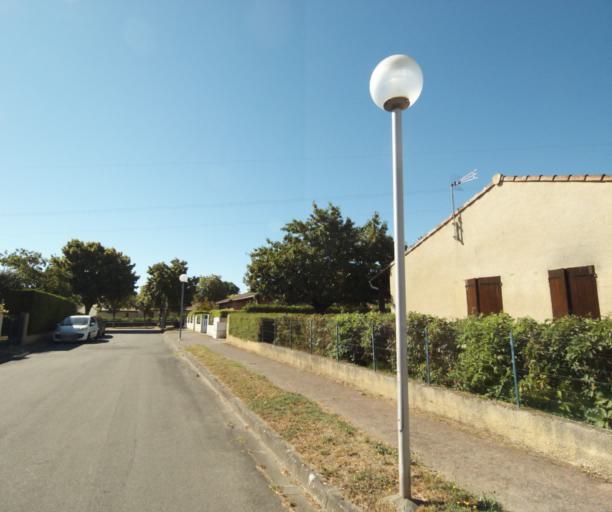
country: FR
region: Midi-Pyrenees
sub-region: Departement de la Haute-Garonne
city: Castanet-Tolosan
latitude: 43.5208
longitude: 1.5023
